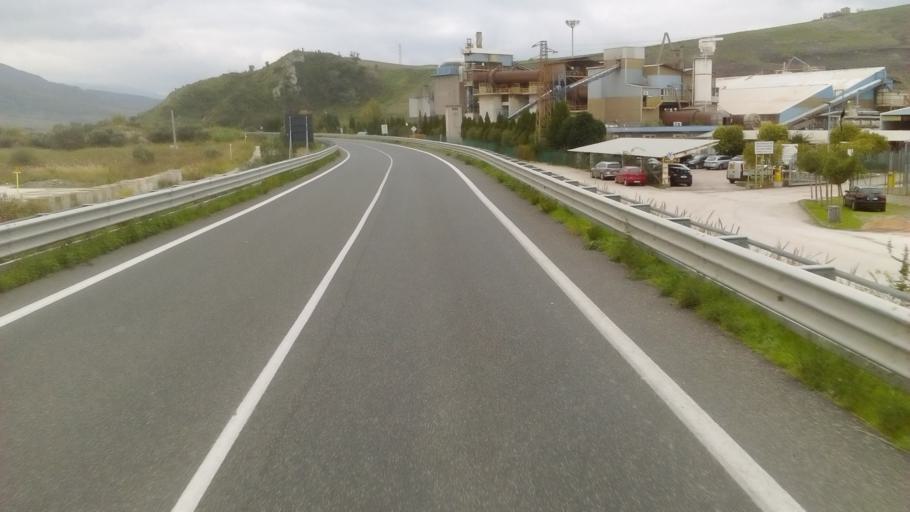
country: IT
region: Abruzzo
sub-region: Provincia di Chieti
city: Lentella
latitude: 41.9954
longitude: 14.7140
